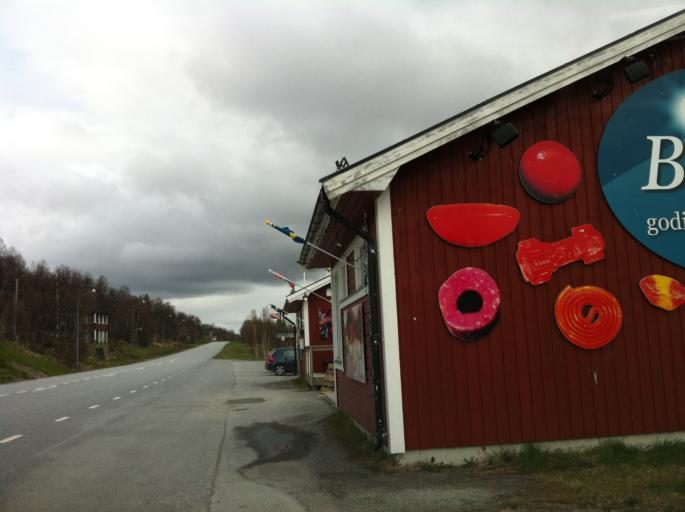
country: NO
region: Sor-Trondelag
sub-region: Tydal
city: Aas
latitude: 62.5457
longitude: 12.3269
